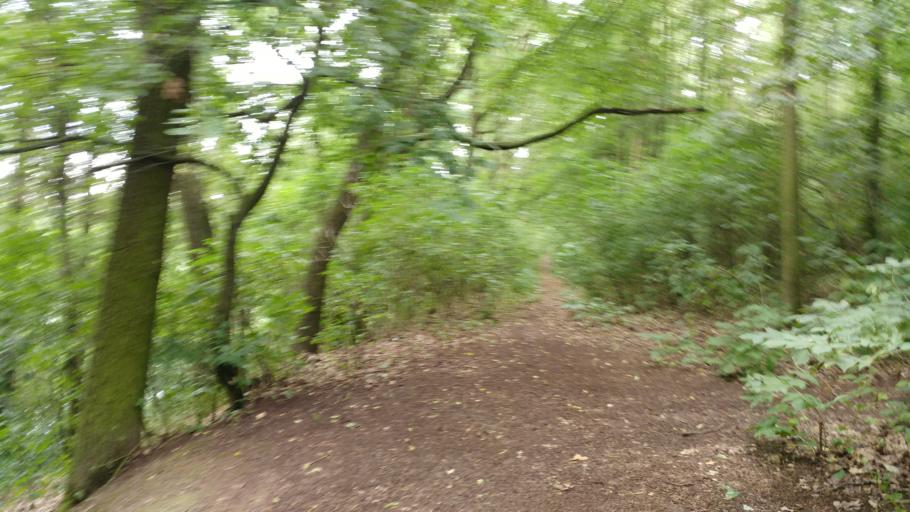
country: CZ
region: Central Bohemia
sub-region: Okres Praha-Zapad
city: Pruhonice
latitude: 50.0360
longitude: 14.5433
